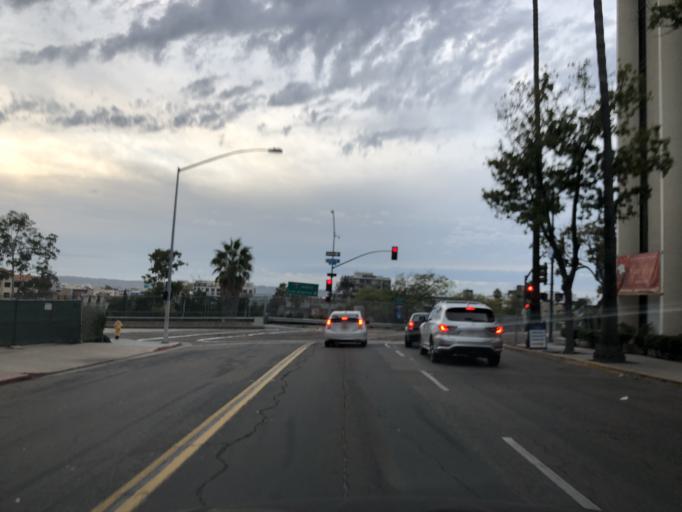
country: US
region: California
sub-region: San Diego County
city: San Diego
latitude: 32.7241
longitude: -117.1635
